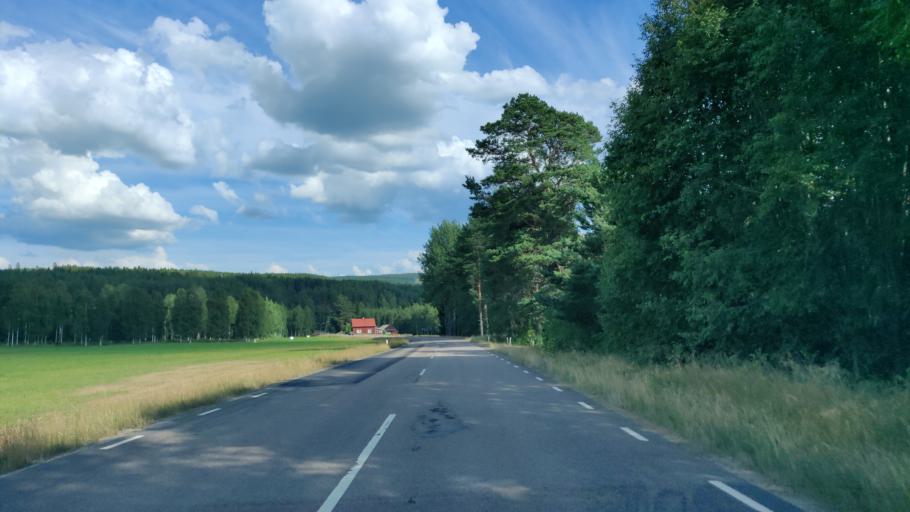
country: SE
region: Vaermland
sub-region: Hagfors Kommun
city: Ekshaerad
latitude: 60.1777
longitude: 13.5186
